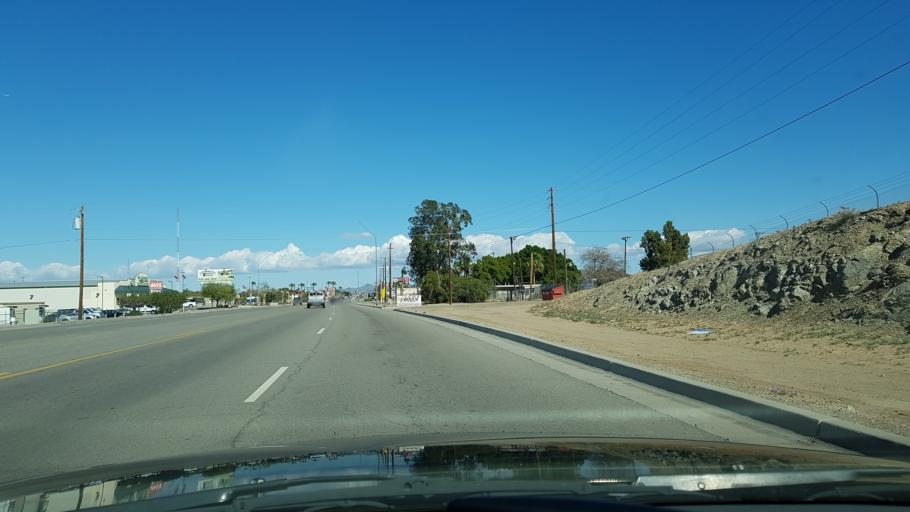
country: US
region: Arizona
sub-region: Yuma County
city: Yuma
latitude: 32.6711
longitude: -114.5986
